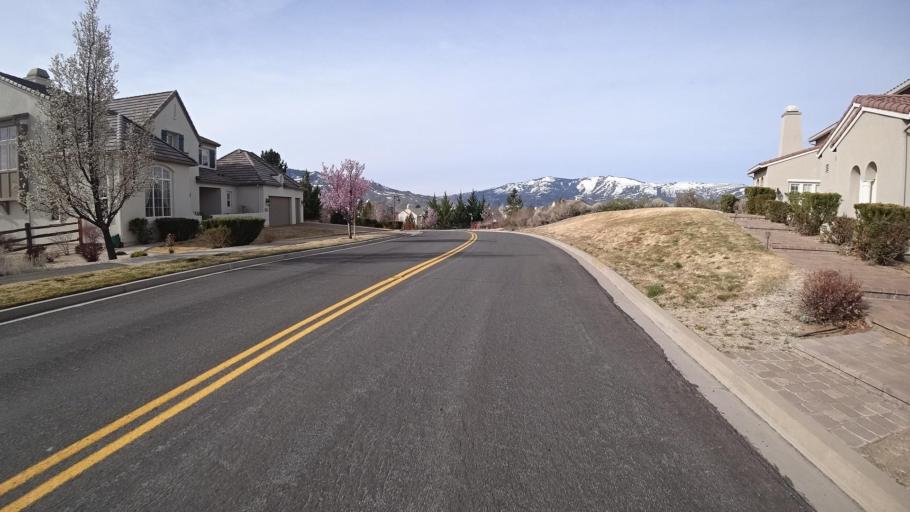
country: US
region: Nevada
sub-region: Washoe County
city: Mogul
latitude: 39.5351
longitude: -119.9379
